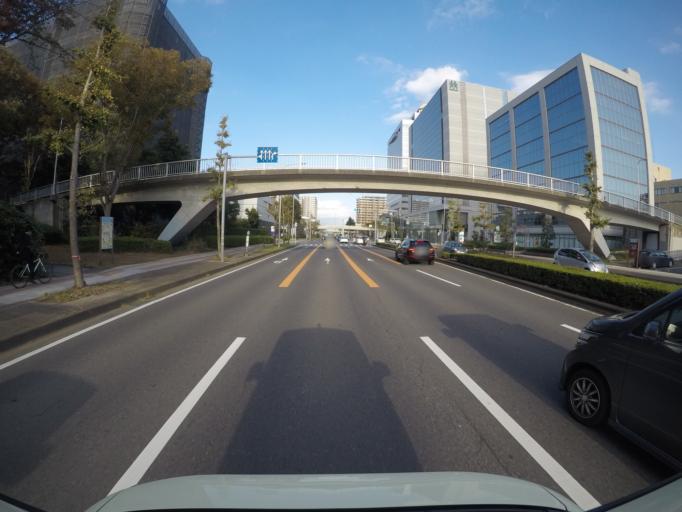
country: JP
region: Ibaraki
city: Naka
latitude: 36.0793
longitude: 140.1106
